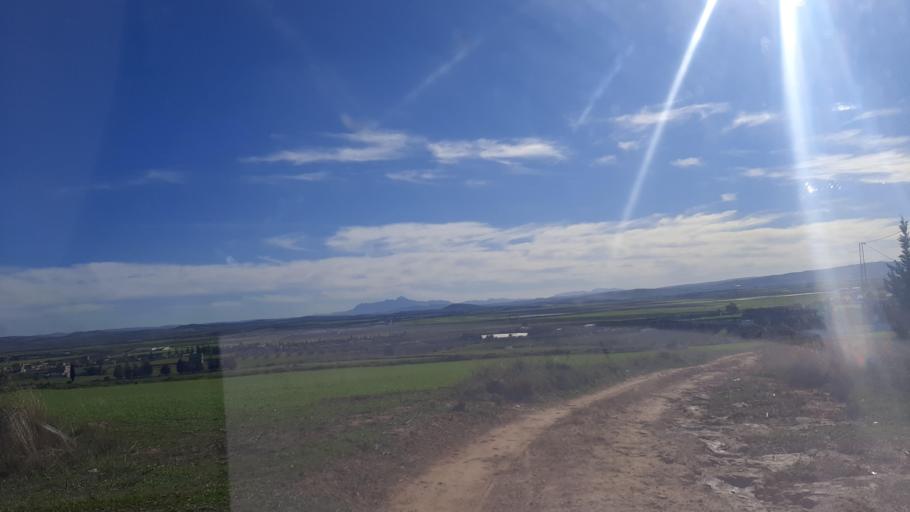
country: TN
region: Tunis
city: Oued Lill
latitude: 36.7649
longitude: 9.9856
